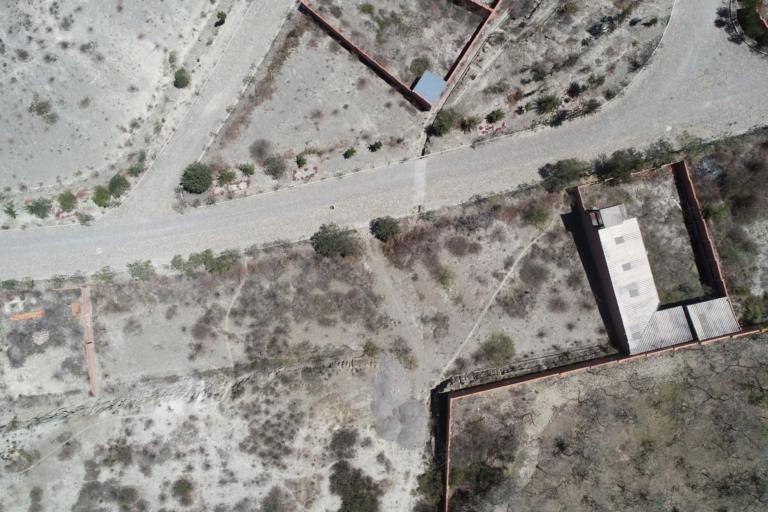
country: BO
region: La Paz
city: La Paz
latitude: -16.6287
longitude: -68.0577
